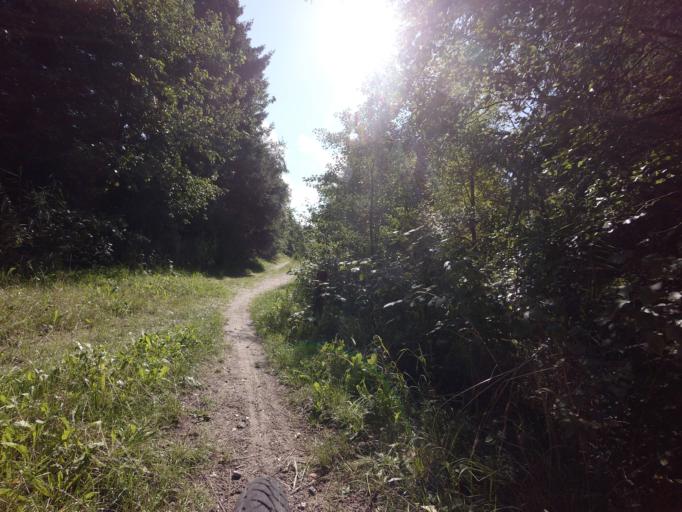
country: DK
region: North Denmark
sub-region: Hjorring Kommune
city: Hirtshals
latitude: 57.5787
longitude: 10.0067
